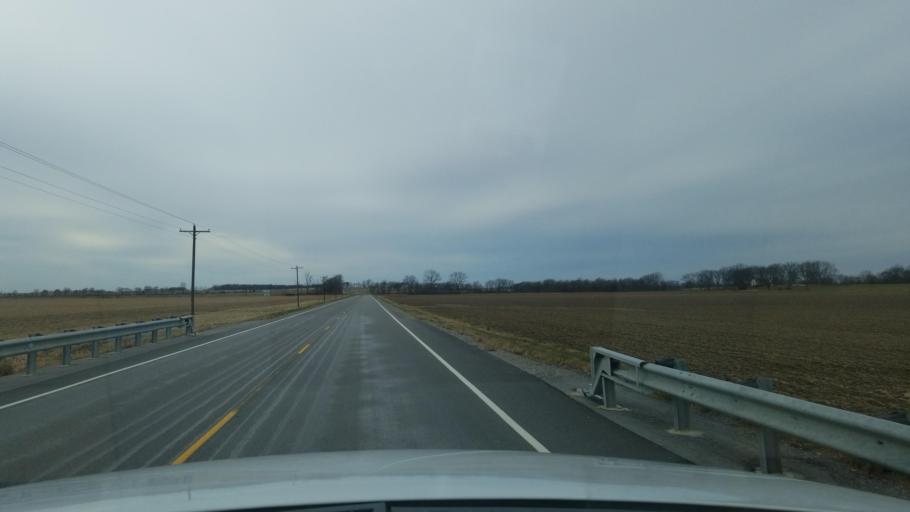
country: US
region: Illinois
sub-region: White County
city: Norris City
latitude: 37.9077
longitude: -88.1727
